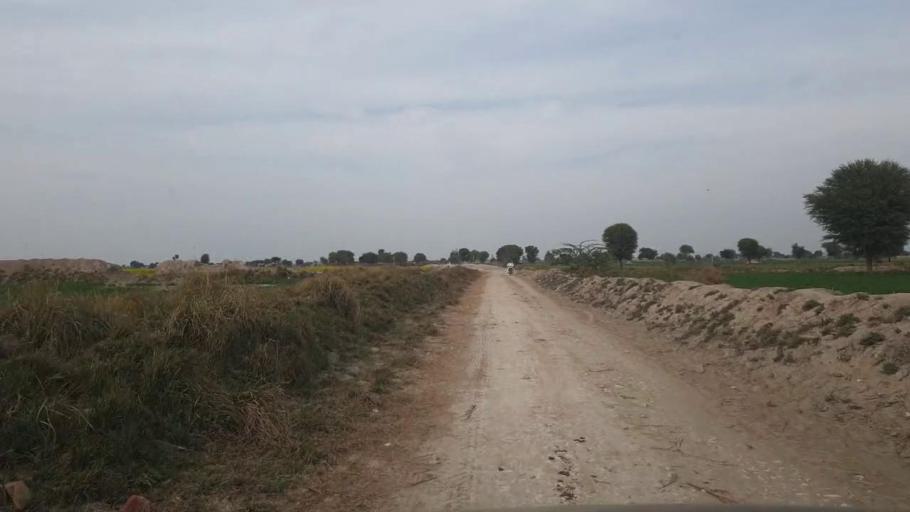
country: PK
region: Sindh
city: Shahpur Chakar
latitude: 26.1188
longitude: 68.5102
